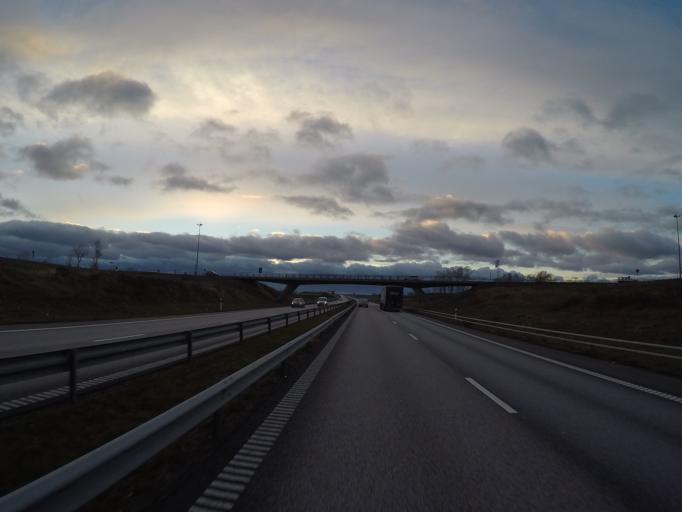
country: SE
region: Skane
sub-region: Kristianstads Kommun
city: Fjalkinge
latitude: 56.0339
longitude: 14.2665
